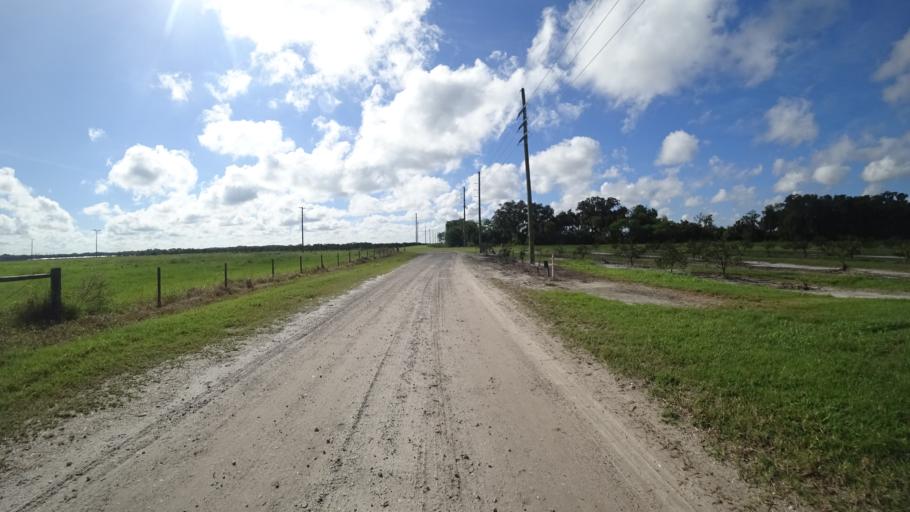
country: US
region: Florida
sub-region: Manatee County
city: Ellenton
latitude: 27.5877
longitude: -82.4746
